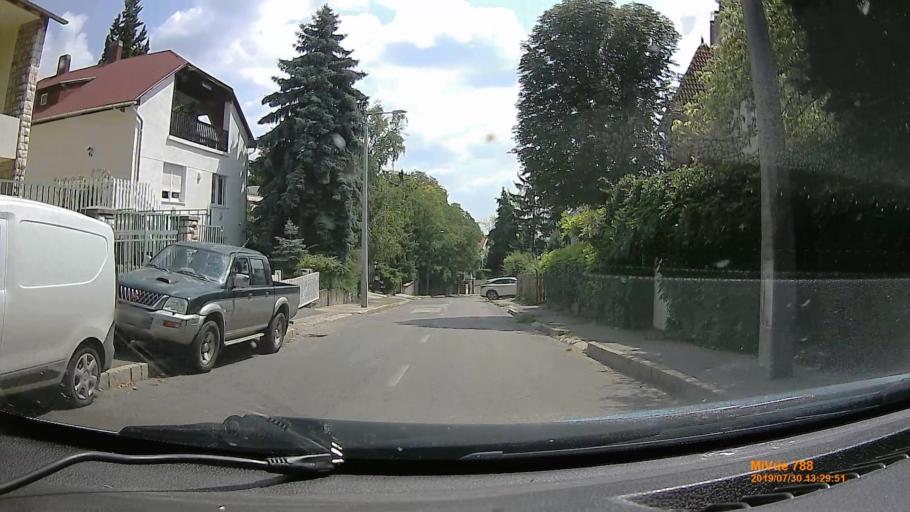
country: HU
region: Baranya
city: Pecs
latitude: 46.0831
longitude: 18.2196
